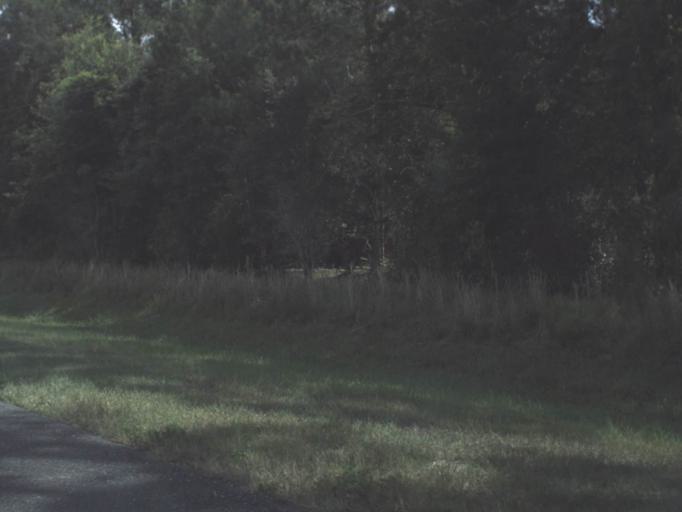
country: US
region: Florida
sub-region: Levy County
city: Chiefland
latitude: 29.4056
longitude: -82.8165
